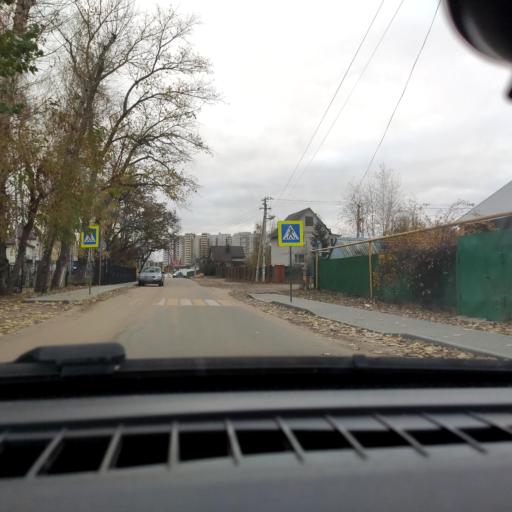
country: RU
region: Voronezj
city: Podgornoye
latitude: 51.7308
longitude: 39.1598
